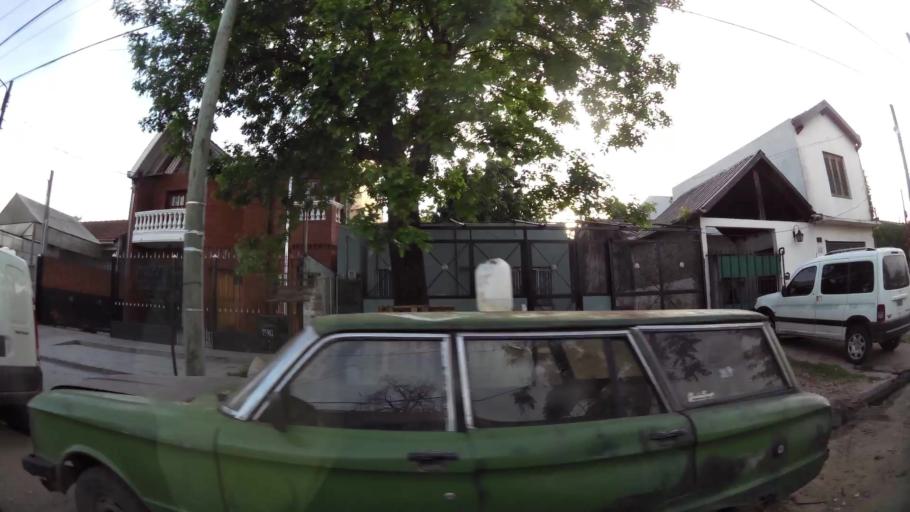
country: AR
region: Buenos Aires
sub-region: Partido de Almirante Brown
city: Adrogue
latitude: -34.7875
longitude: -58.3476
